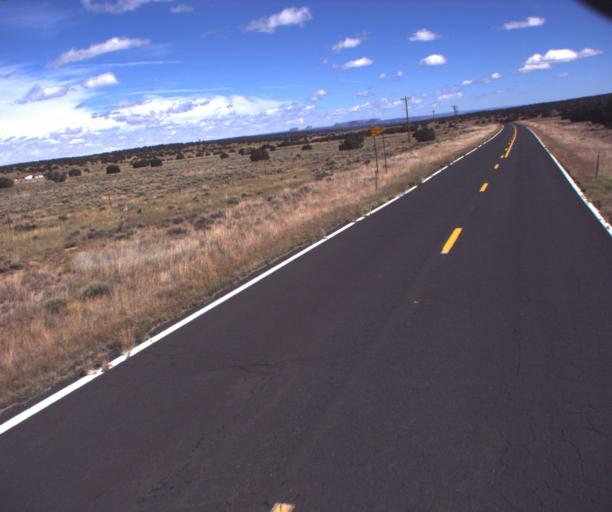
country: US
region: New Mexico
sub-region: McKinley County
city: Zuni Pueblo
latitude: 34.9909
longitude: -109.1067
